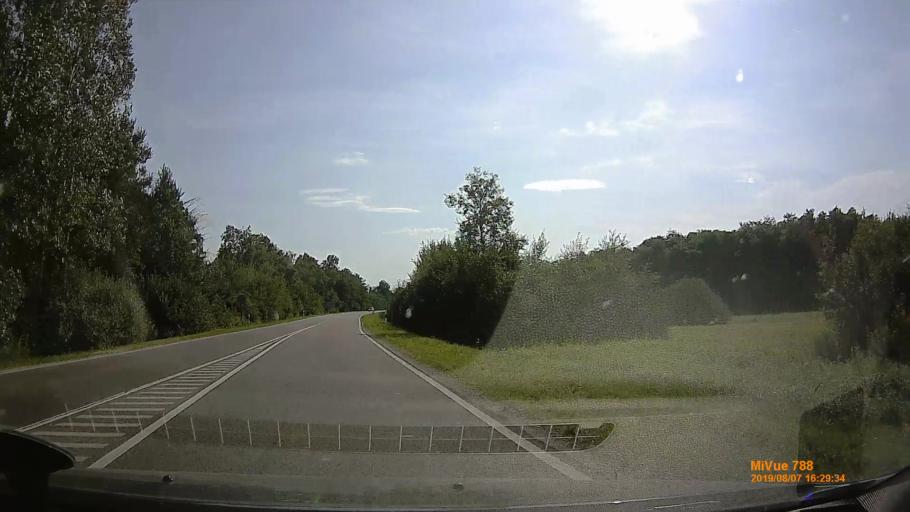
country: HU
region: Zala
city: Lenti
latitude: 46.6791
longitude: 16.5272
